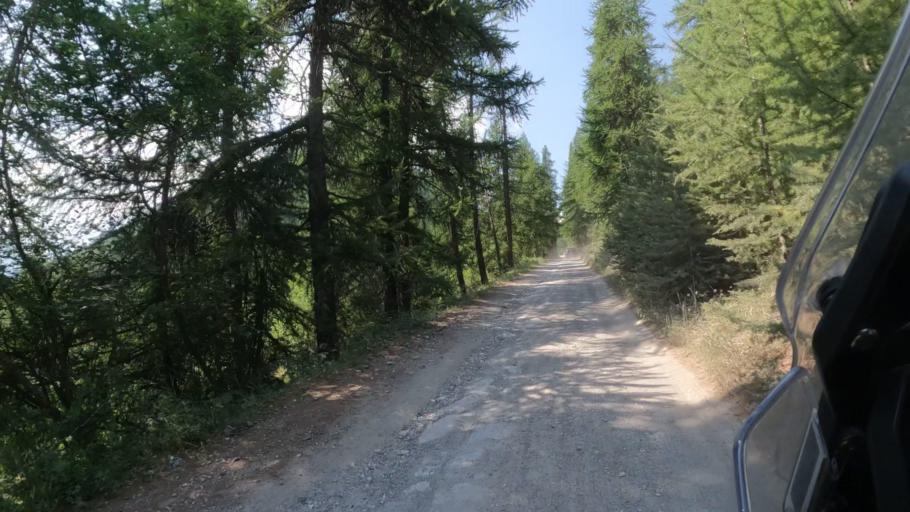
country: IT
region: Piedmont
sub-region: Provincia di Torino
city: Cesana Torinese
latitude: 44.9244
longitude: 6.8117
